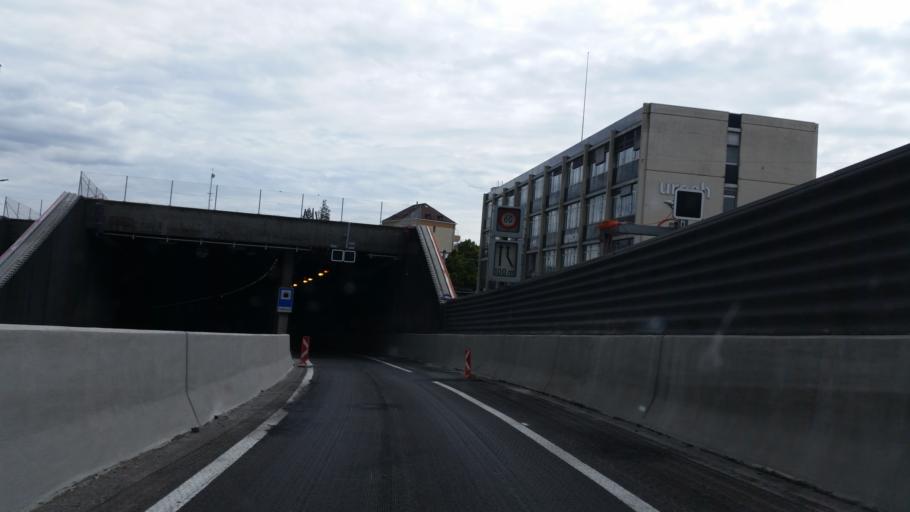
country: CH
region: Neuchatel
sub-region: Boudry District
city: Peseux
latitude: 46.9885
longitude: 6.9091
